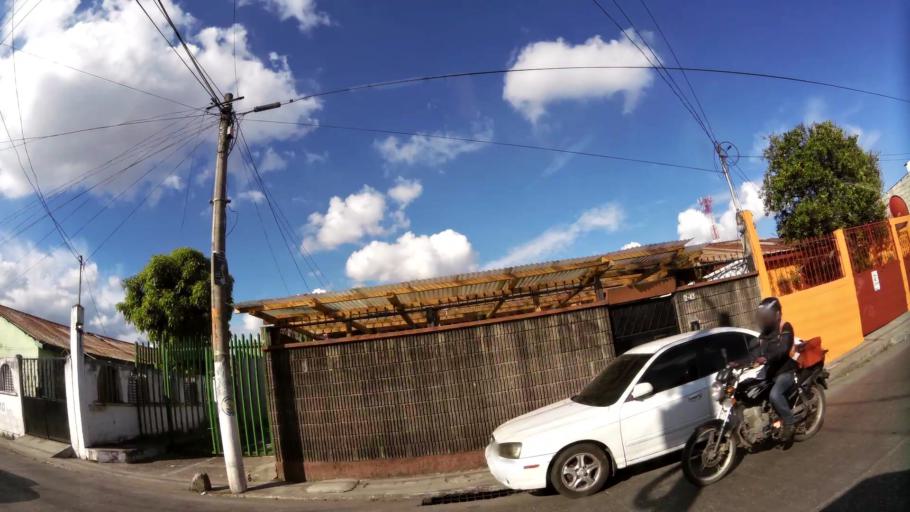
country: GT
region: Guatemala
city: Villa Nueva
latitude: 14.5220
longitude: -90.5770
